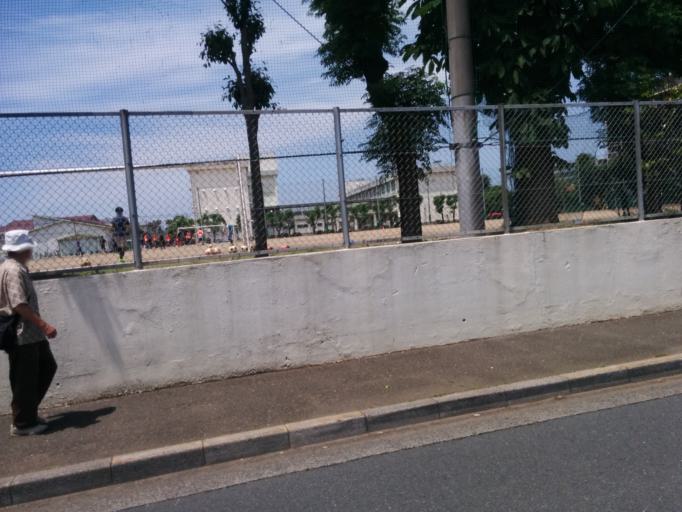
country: JP
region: Tokyo
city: Higashimurayama-shi
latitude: 35.7596
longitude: 139.4783
